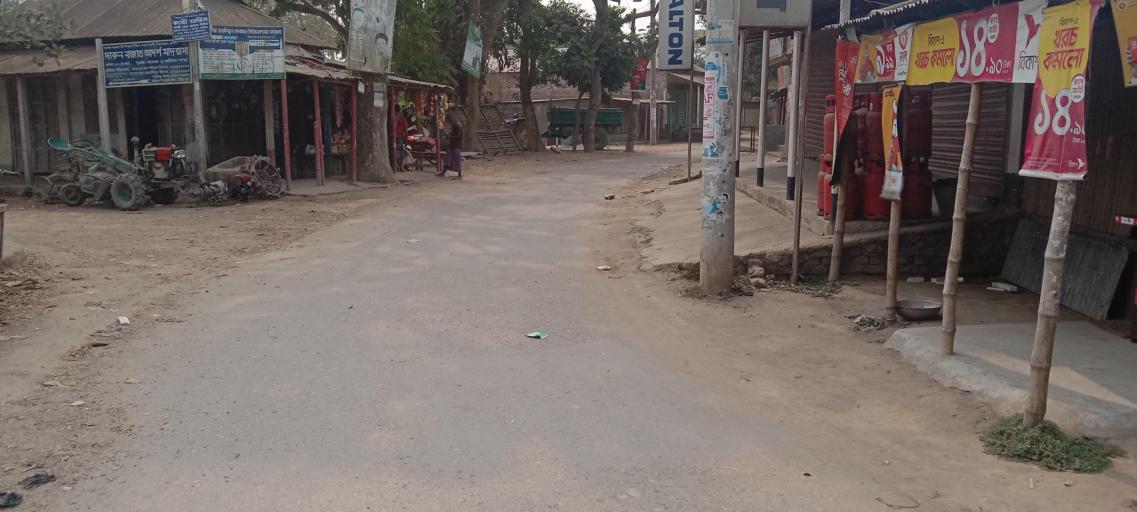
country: BD
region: Dhaka
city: Gafargaon
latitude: 24.4557
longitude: 90.4637
